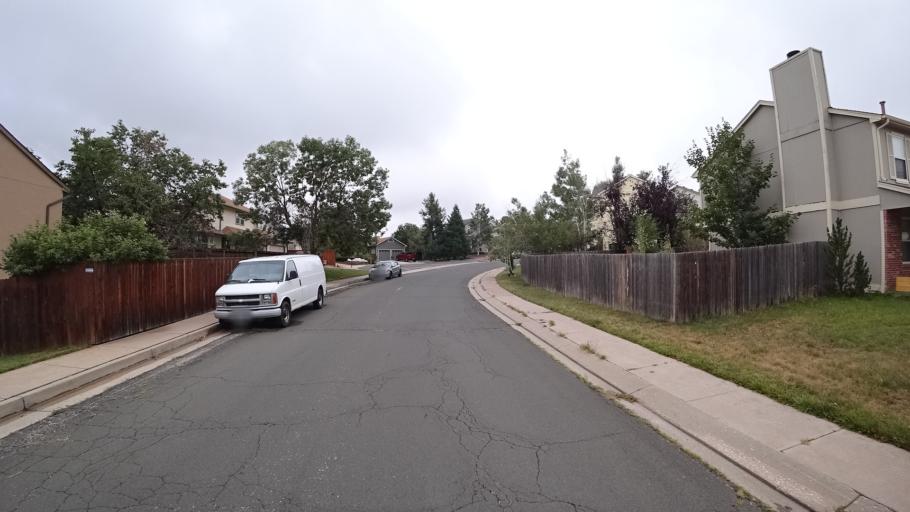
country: US
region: Colorado
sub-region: El Paso County
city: Cimarron Hills
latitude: 38.9271
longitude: -104.7647
